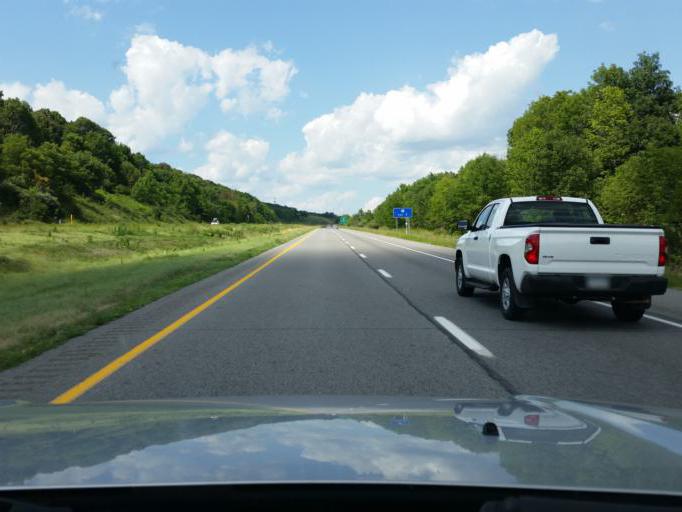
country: US
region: Pennsylvania
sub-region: Bedford County
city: Bedford
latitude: 40.1233
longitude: -78.5191
